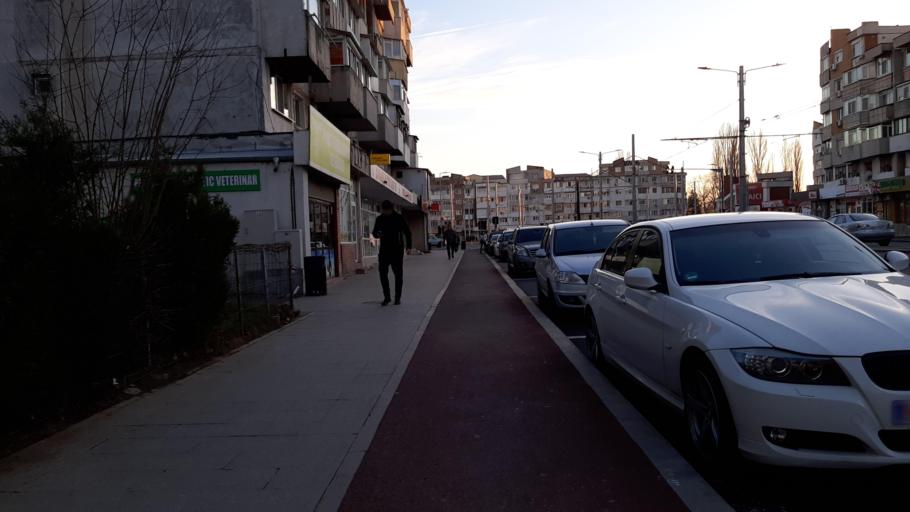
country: RO
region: Galati
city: Galati
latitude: 45.4414
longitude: 28.0212
